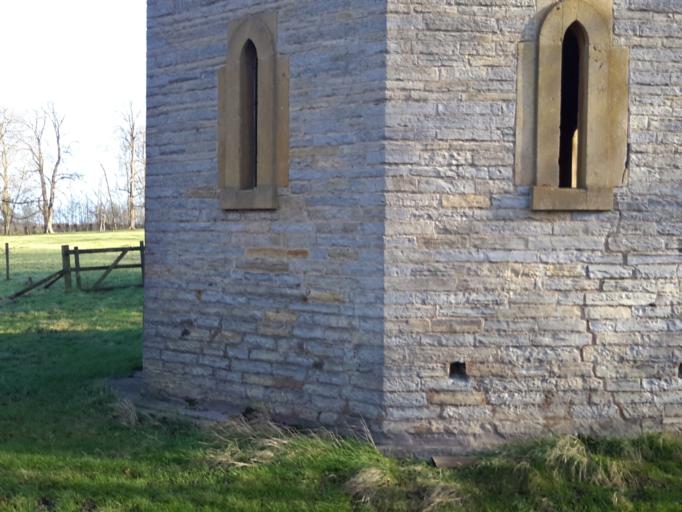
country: GB
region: England
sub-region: Worcestershire
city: Evesham
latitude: 52.1098
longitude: -1.9572
